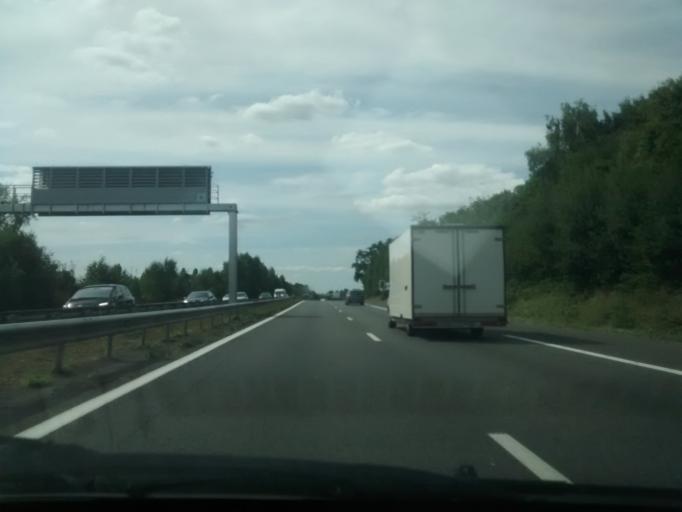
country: FR
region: Brittany
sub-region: Departement d'Ille-et-Vilaine
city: Pace
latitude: 48.1449
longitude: -1.7826
